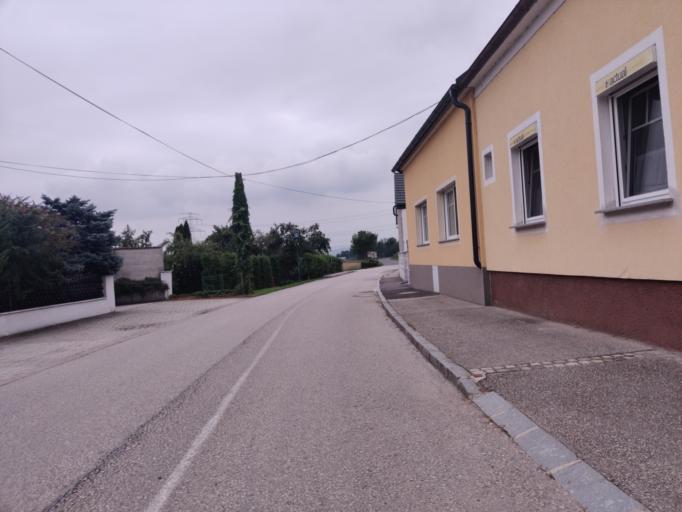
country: AT
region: Lower Austria
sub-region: Politischer Bezirk Tulln
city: Langenrohr
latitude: 48.3281
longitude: 15.9845
